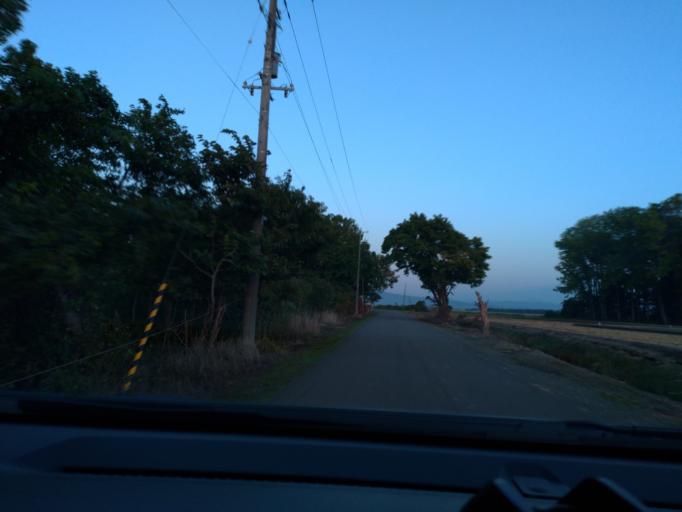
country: JP
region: Hokkaido
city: Iwamizawa
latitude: 43.3291
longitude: 141.7130
